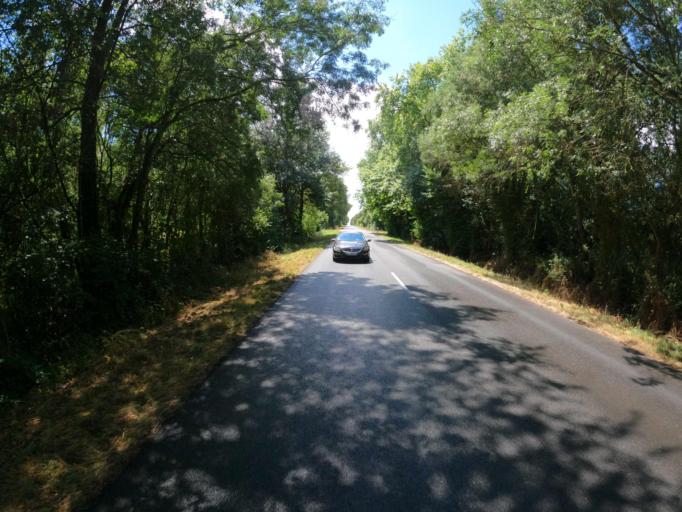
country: FR
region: Pays de la Loire
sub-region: Departement de Maine-et-Loire
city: Champigne
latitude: 47.6332
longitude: -0.5802
